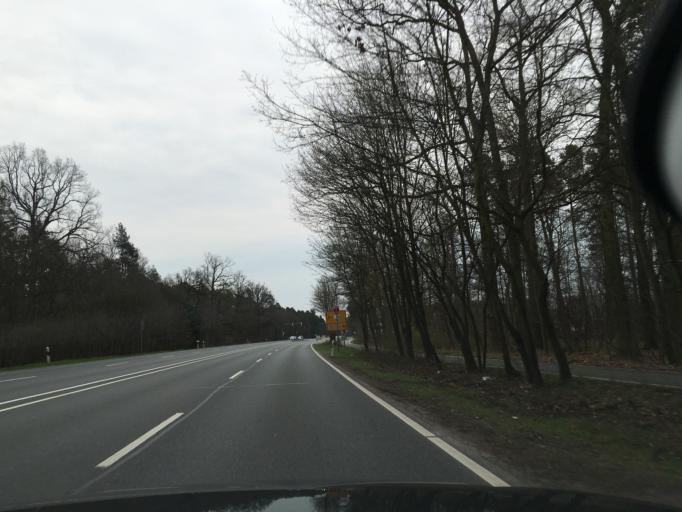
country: DE
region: Bavaria
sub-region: Regierungsbezirk Mittelfranken
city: Nuernberg
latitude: 49.4289
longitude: 11.1412
